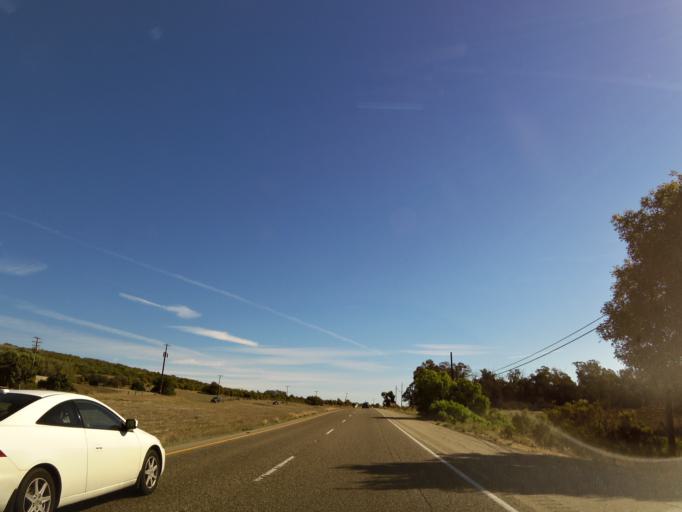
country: US
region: California
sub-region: Santa Barbara County
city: Isla Vista
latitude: 34.4549
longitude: -119.9702
